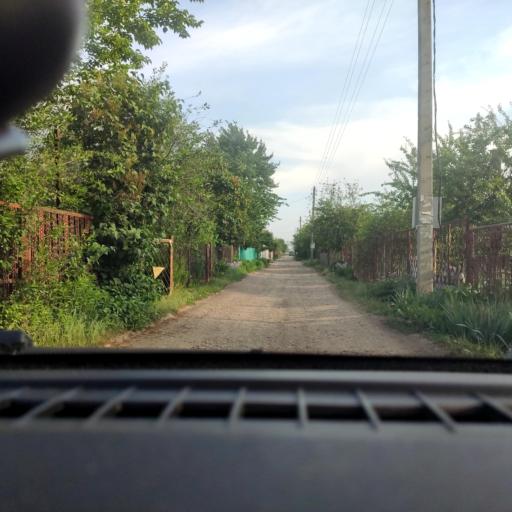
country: RU
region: Samara
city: Tol'yatti
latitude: 53.5921
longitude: 49.3236
